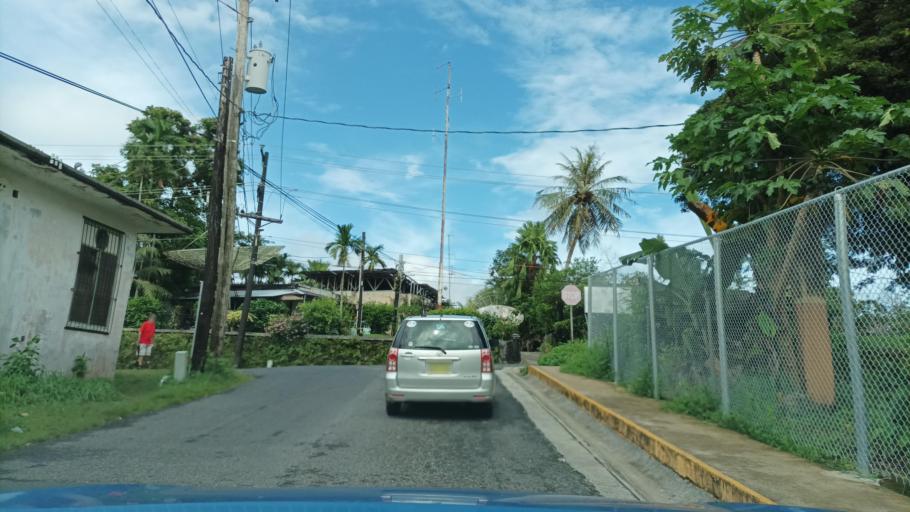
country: FM
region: Pohnpei
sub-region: Kolonia Municipality
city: Kolonia
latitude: 6.9595
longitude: 158.2107
